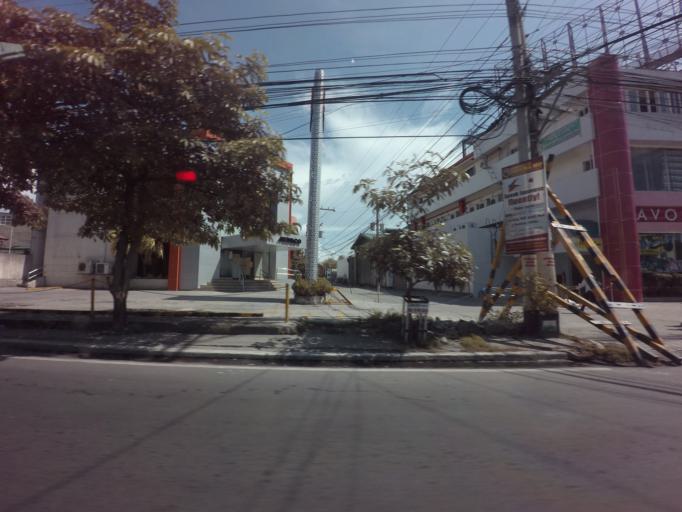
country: PH
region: Calabarzon
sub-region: Province of Rizal
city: Las Pinas
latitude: 14.4487
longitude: 120.9832
